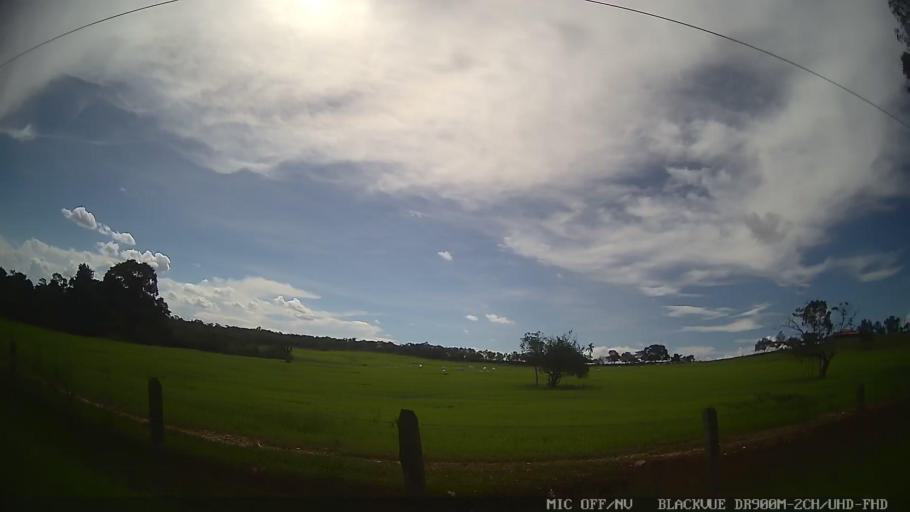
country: BR
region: Sao Paulo
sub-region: Conchas
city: Conchas
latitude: -22.9860
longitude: -47.9917
